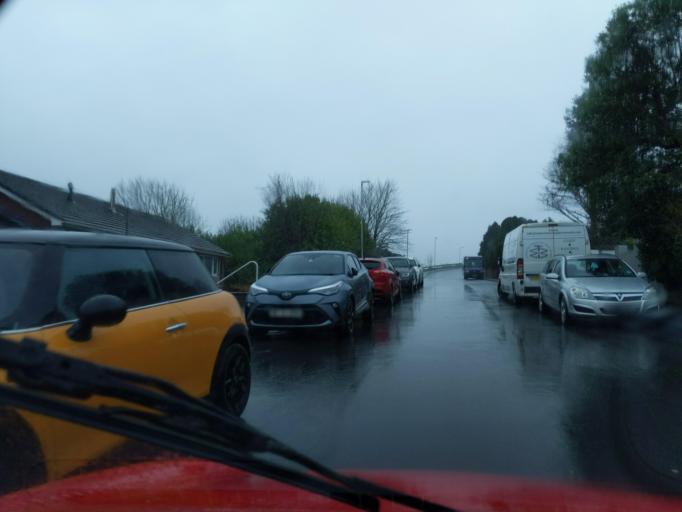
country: GB
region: England
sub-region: Plymouth
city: Plymstock
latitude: 50.4040
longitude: -4.1074
